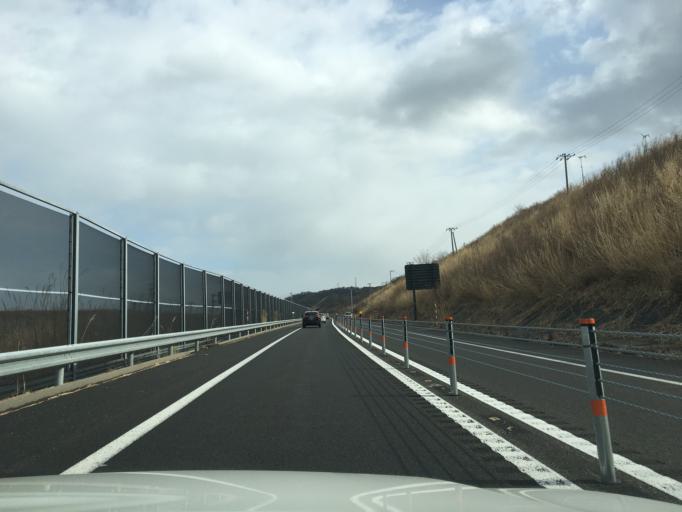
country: JP
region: Yamagata
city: Yuza
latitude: 39.3051
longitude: 139.9793
